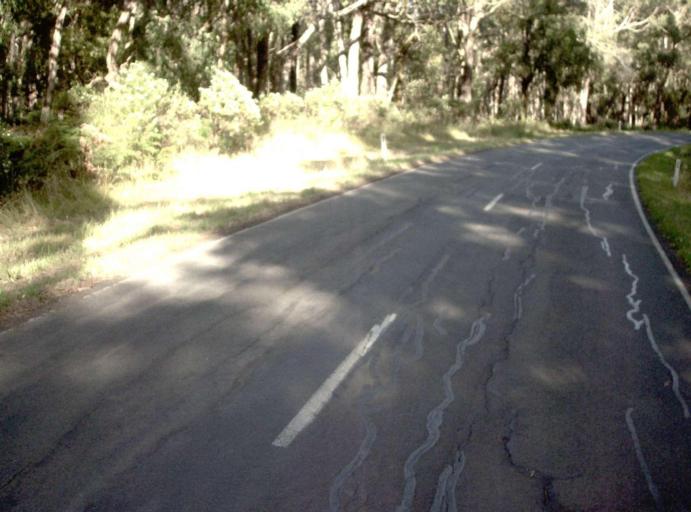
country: AU
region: Victoria
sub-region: Latrobe
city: Morwell
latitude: -38.3988
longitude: 146.2748
